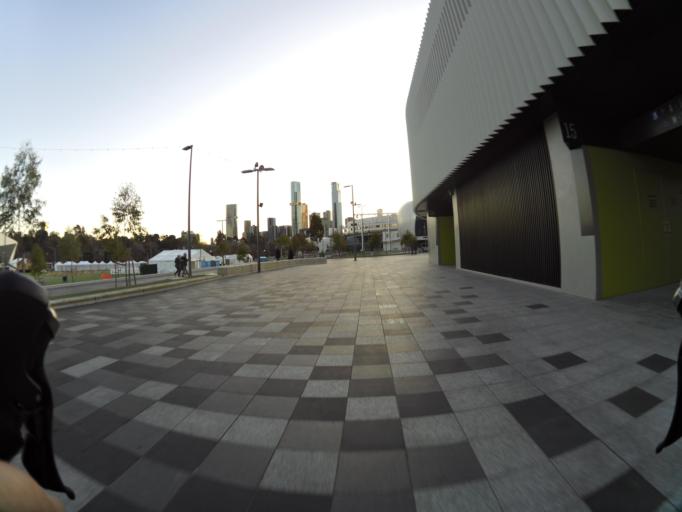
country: AU
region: Victoria
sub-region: Melbourne
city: East Melbourne
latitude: -37.8223
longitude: 144.9807
